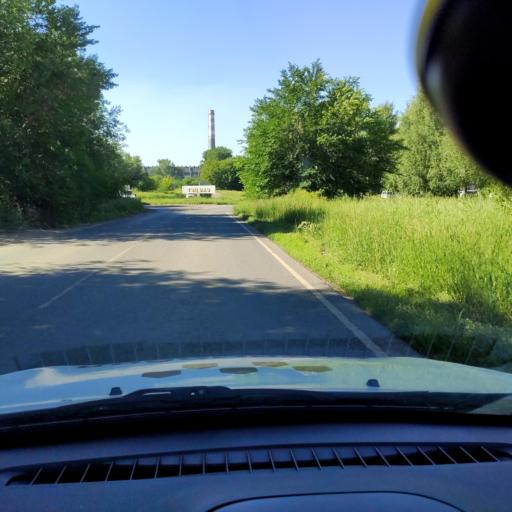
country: RU
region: Samara
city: Tol'yatti
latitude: 53.5753
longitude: 49.2547
